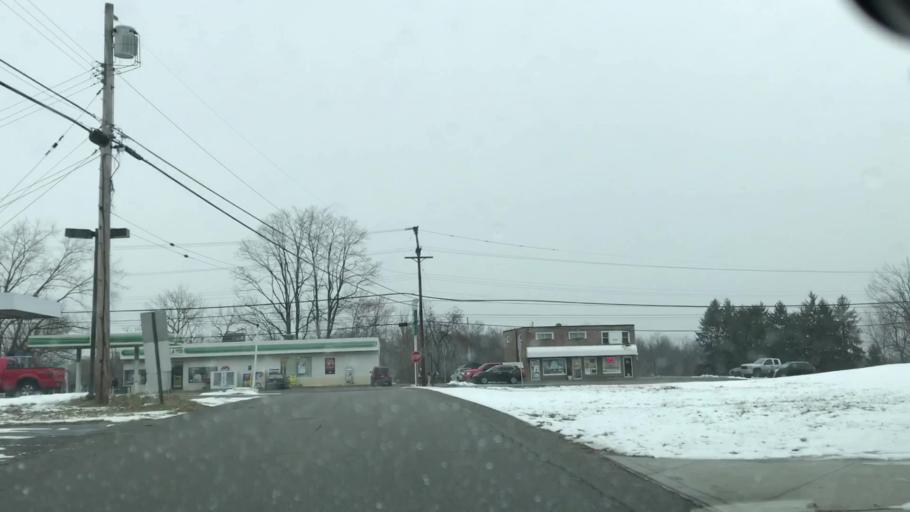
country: US
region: Pennsylvania
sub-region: Beaver County
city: Industry
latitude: 40.7037
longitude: -80.4015
